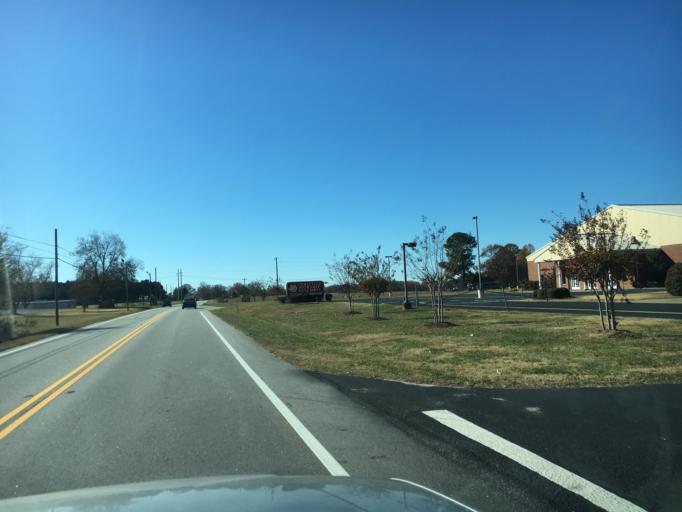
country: US
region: Georgia
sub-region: Hart County
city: Hartwell
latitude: 34.3181
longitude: -82.9859
